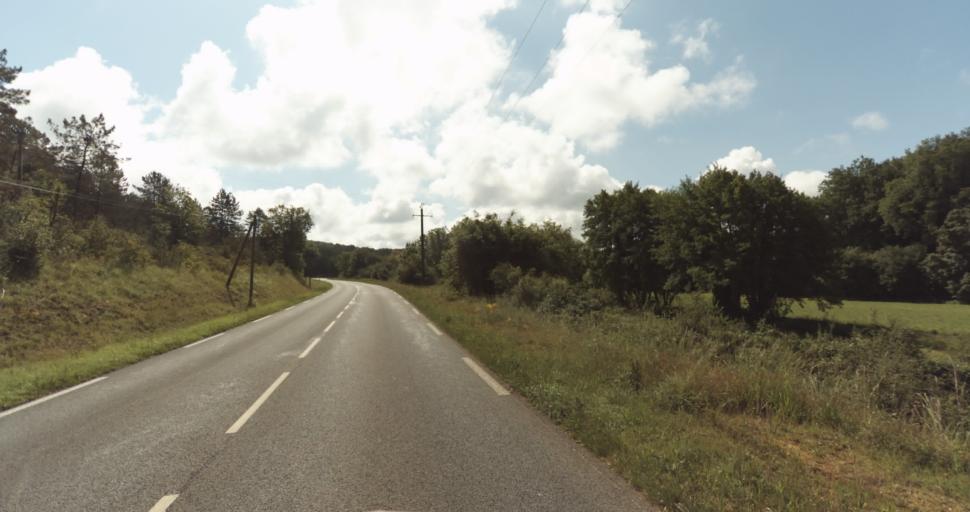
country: FR
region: Aquitaine
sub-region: Departement de la Dordogne
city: Beaumont-du-Perigord
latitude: 44.8462
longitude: 0.8441
